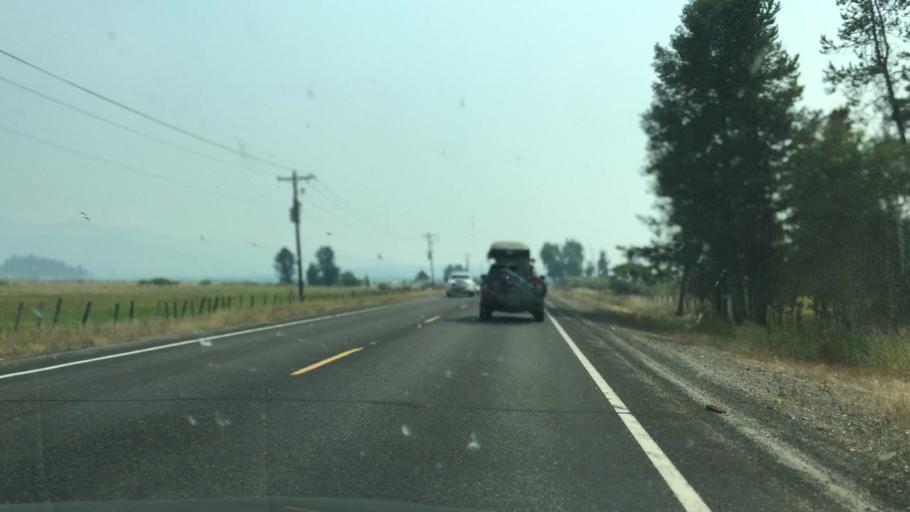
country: US
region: Idaho
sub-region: Valley County
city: Cascade
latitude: 44.4309
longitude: -115.9997
